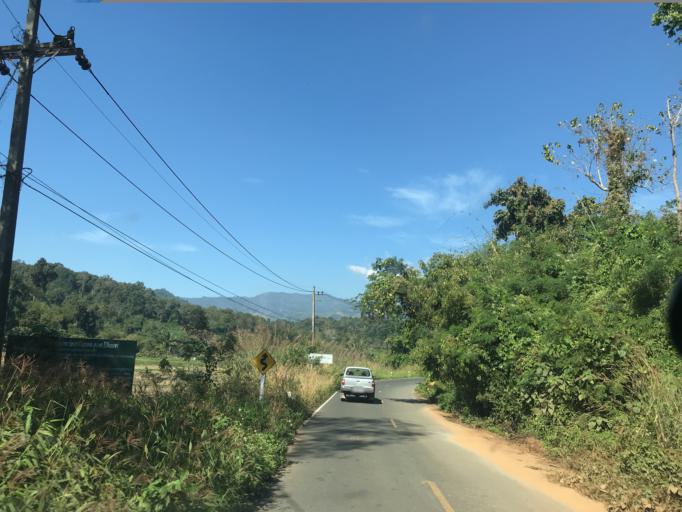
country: TH
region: Chiang Rai
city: Mae Lao
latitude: 19.8091
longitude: 99.6463
